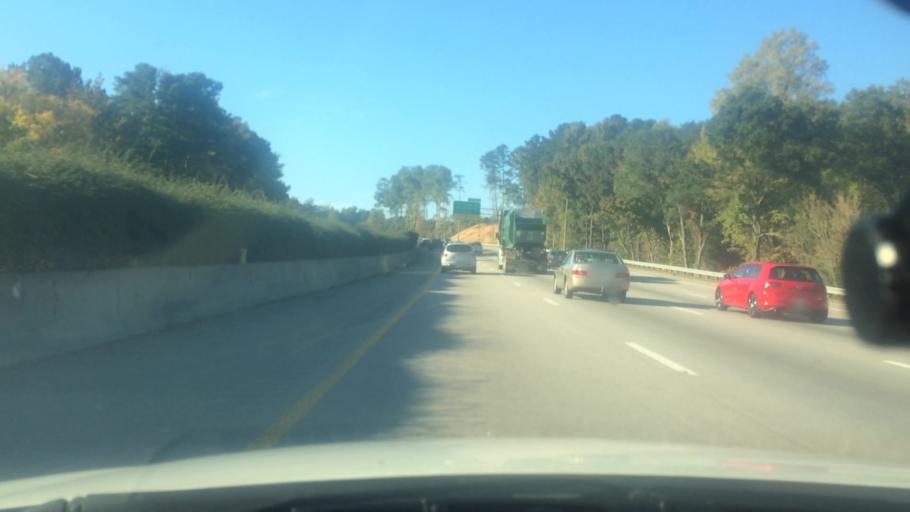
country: US
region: North Carolina
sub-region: Wake County
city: West Raleigh
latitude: 35.8305
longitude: -78.6286
